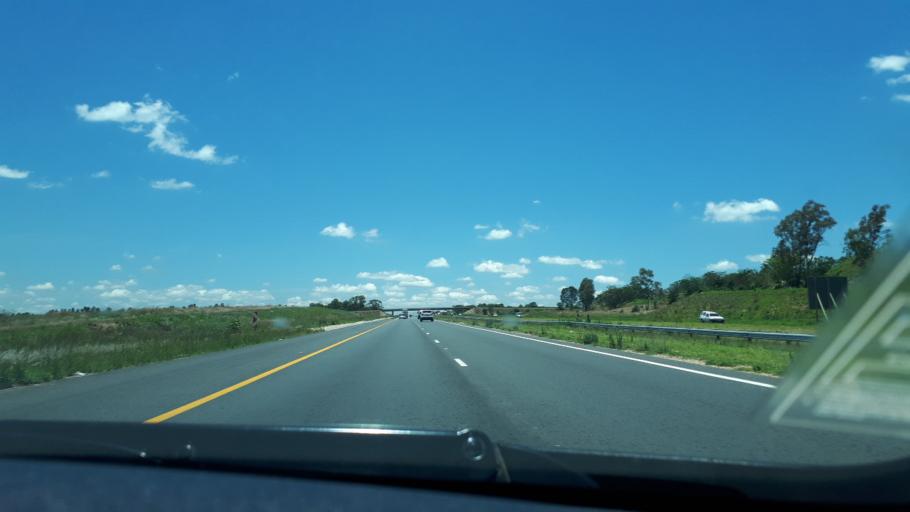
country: ZA
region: Gauteng
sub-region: City of Johannesburg Metropolitan Municipality
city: Diepsloot
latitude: -25.9751
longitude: 27.9372
